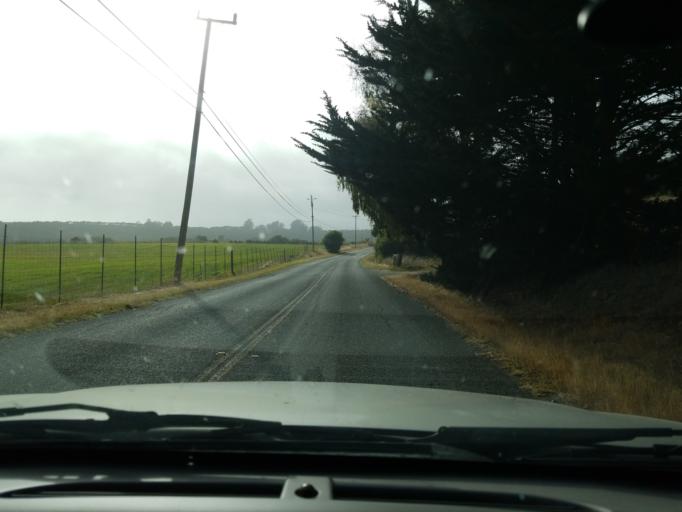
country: US
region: California
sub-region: Monterey County
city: Elkhorn
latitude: 36.8444
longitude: -121.7461
